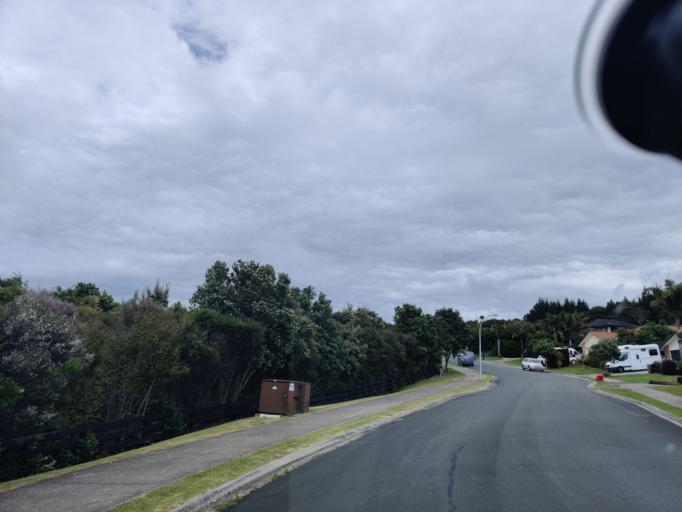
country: NZ
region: Auckland
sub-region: Auckland
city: Rothesay Bay
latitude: -36.5672
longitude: 174.6877
